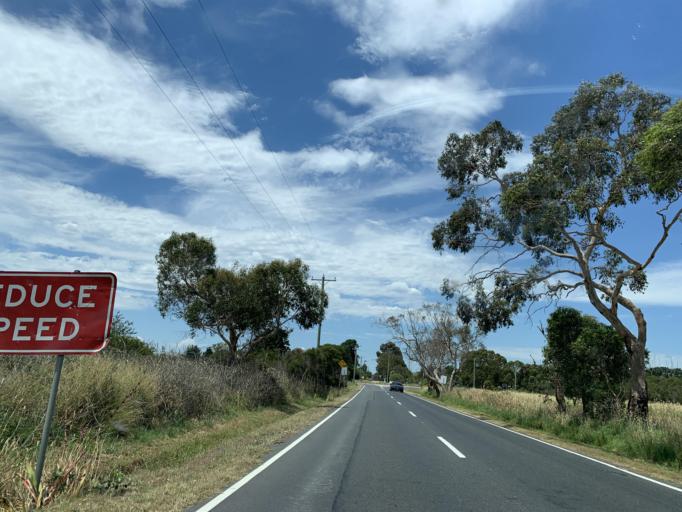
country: AU
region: Victoria
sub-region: Mornington Peninsula
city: Tyabb
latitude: -38.2387
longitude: 145.2315
